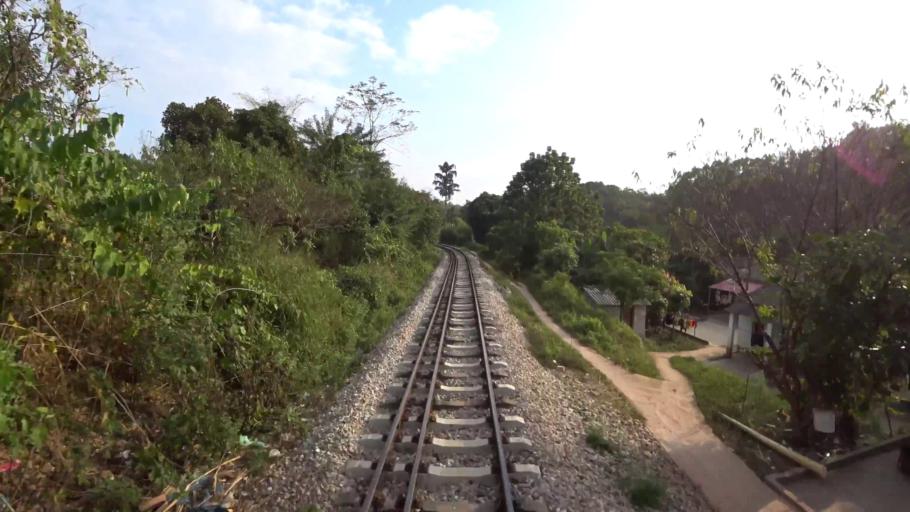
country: VN
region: Lang Son
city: Thi Tran Cao Loc
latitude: 21.9315
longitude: 106.7000
